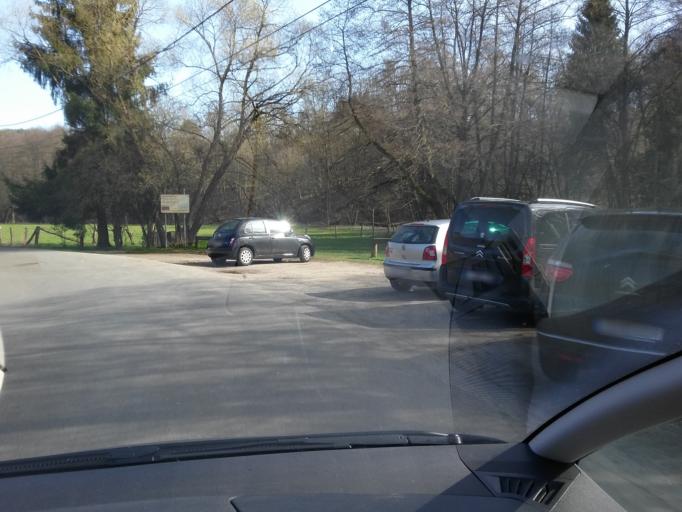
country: BE
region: Wallonia
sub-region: Province du Luxembourg
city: Daverdisse
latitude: 49.9925
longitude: 5.1542
